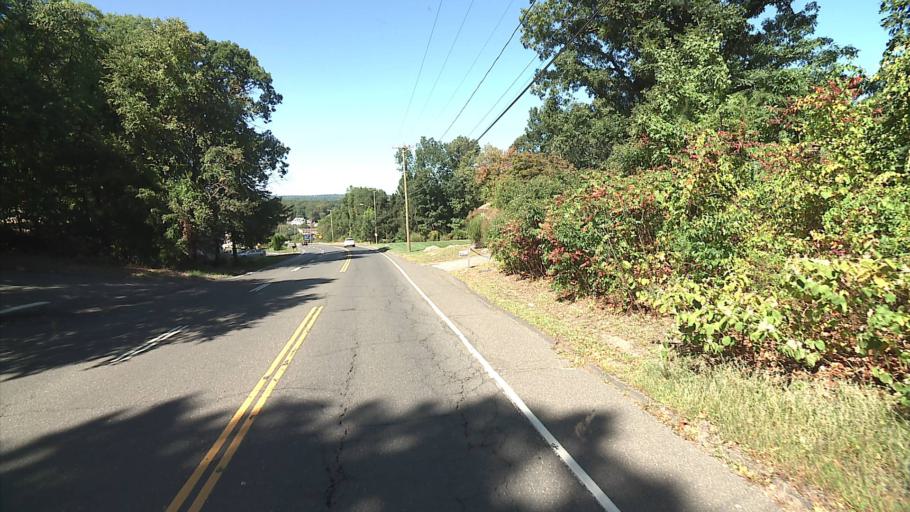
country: US
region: Connecticut
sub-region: New Haven County
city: Waterbury
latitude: 41.5359
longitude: -73.0120
